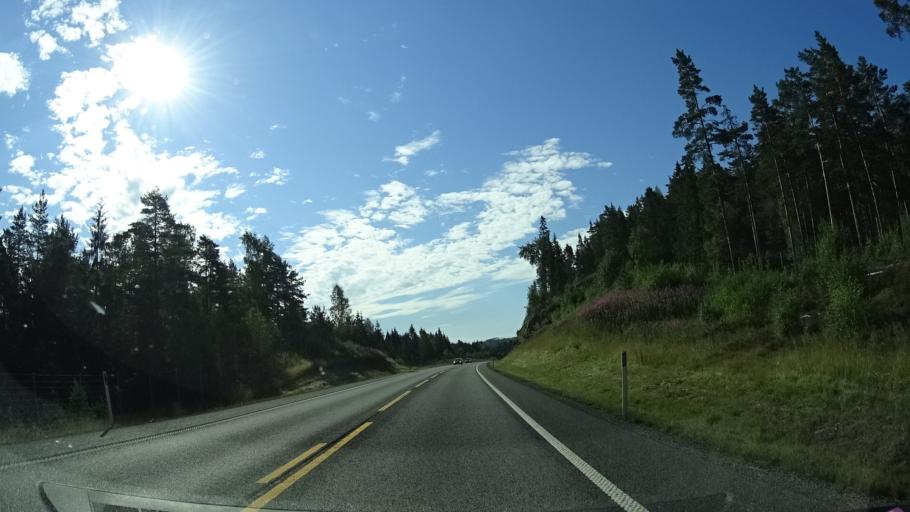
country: NO
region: Ostfold
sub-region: Marker
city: Orje
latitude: 59.5329
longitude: 11.5671
